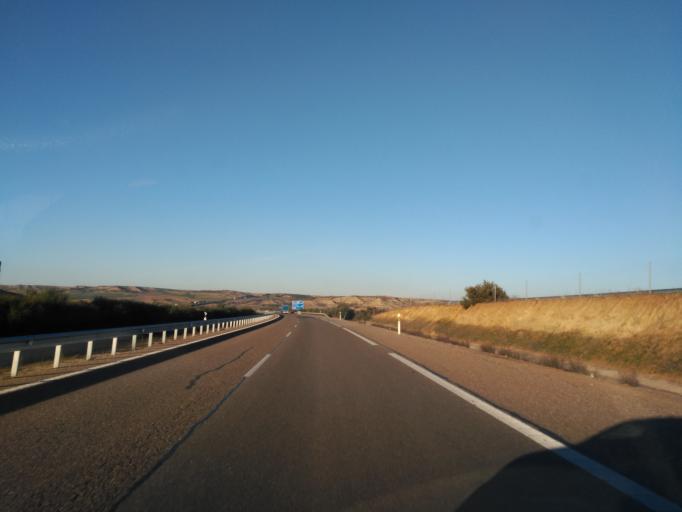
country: ES
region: Castille and Leon
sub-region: Provincia de Zamora
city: Castrillo de la Guarena
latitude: 41.2100
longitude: -5.3242
